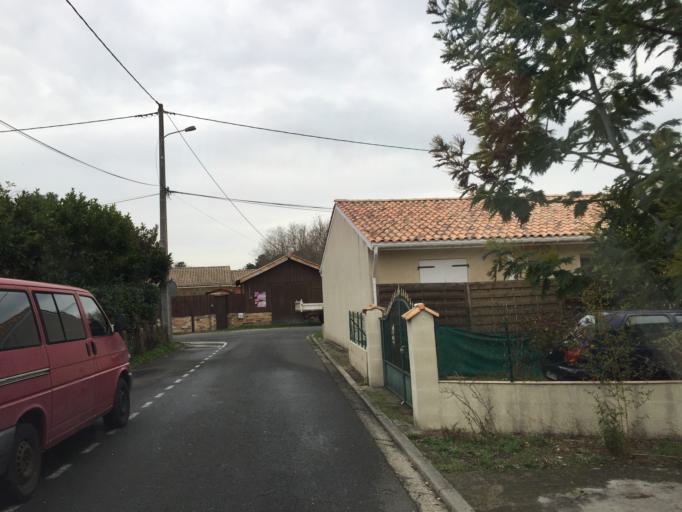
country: FR
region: Aquitaine
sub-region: Departement de la Gironde
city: Carcans
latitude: 45.0783
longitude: -1.0487
